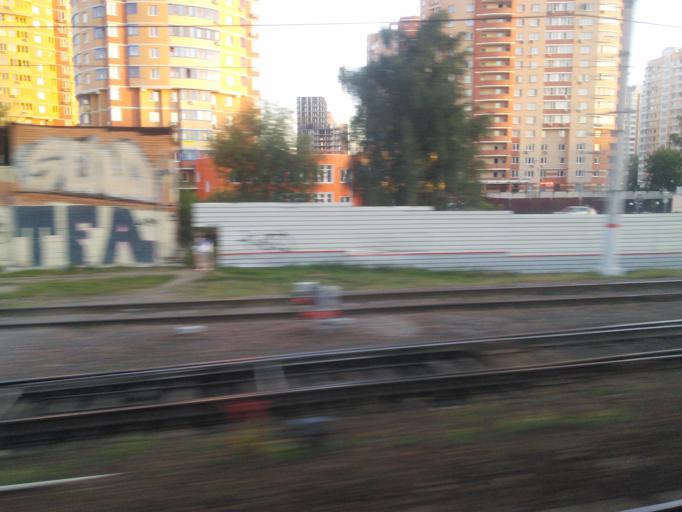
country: RU
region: Moskovskaya
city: Zheleznodorozhnyy
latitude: 55.7521
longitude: 37.9954
